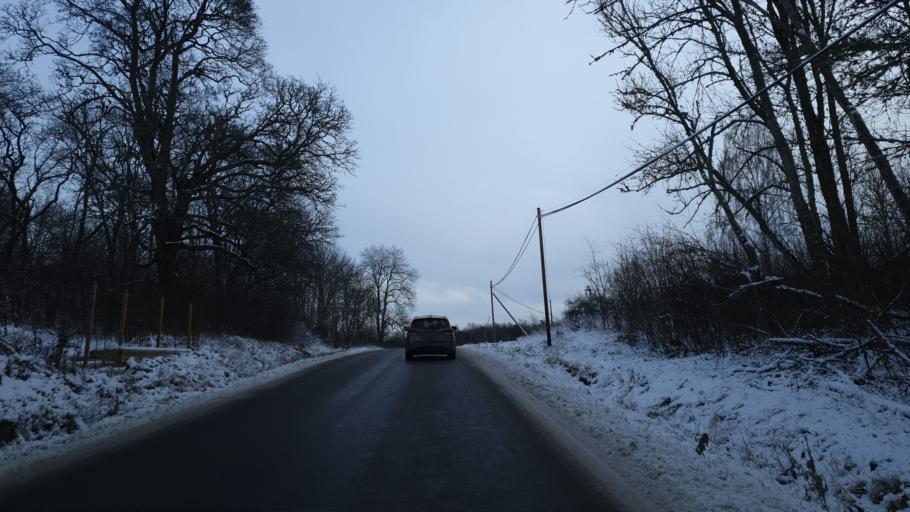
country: SE
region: Uppsala
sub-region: Uppsala Kommun
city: Saevja
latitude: 59.7071
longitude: 17.5970
